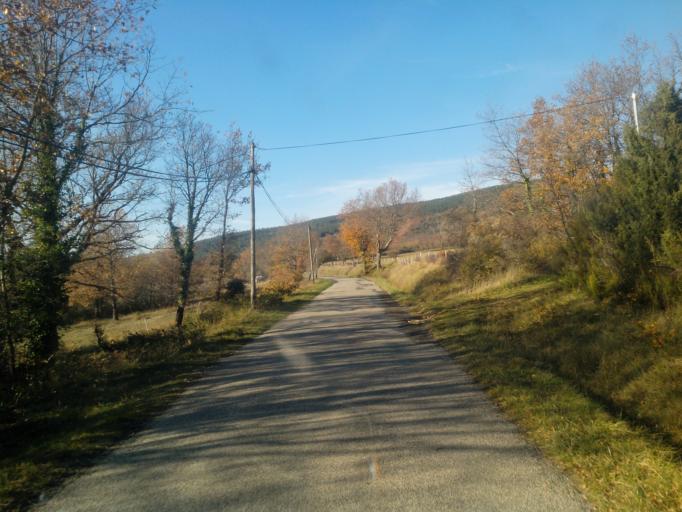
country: FR
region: Languedoc-Roussillon
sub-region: Departement des Pyrenees-Orientales
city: Saint-Paul-de-Fenouillet
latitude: 42.8634
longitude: 2.4266
